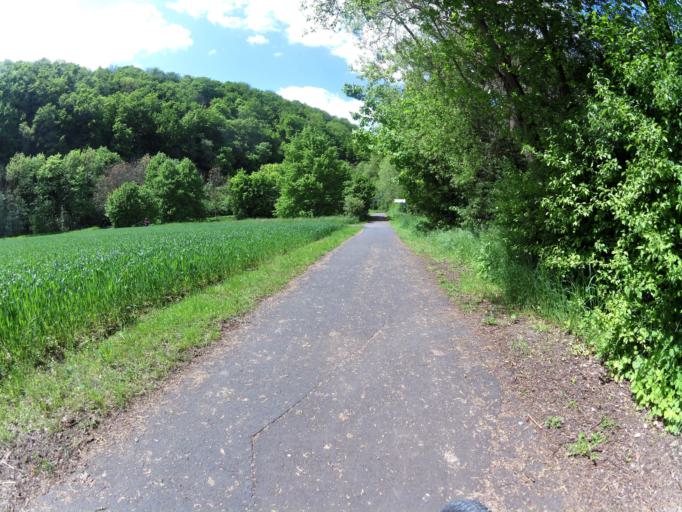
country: DE
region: Thuringia
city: Ebenshausen
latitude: 51.0853
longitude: 10.3079
